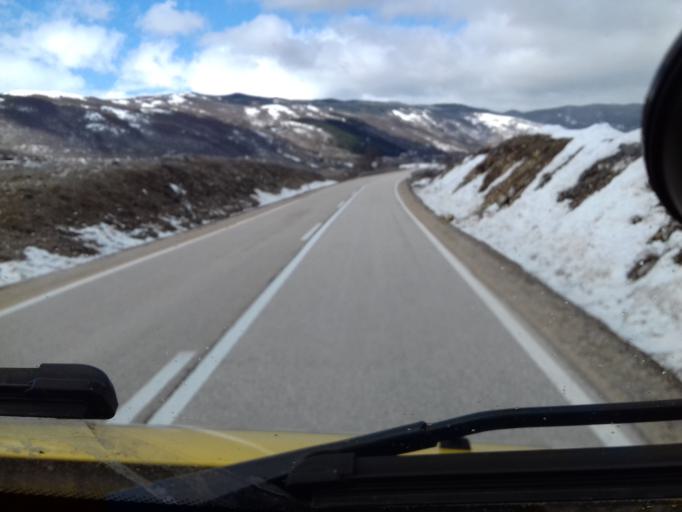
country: BA
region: Federation of Bosnia and Herzegovina
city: Tomislavgrad
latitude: 43.8143
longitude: 17.2009
